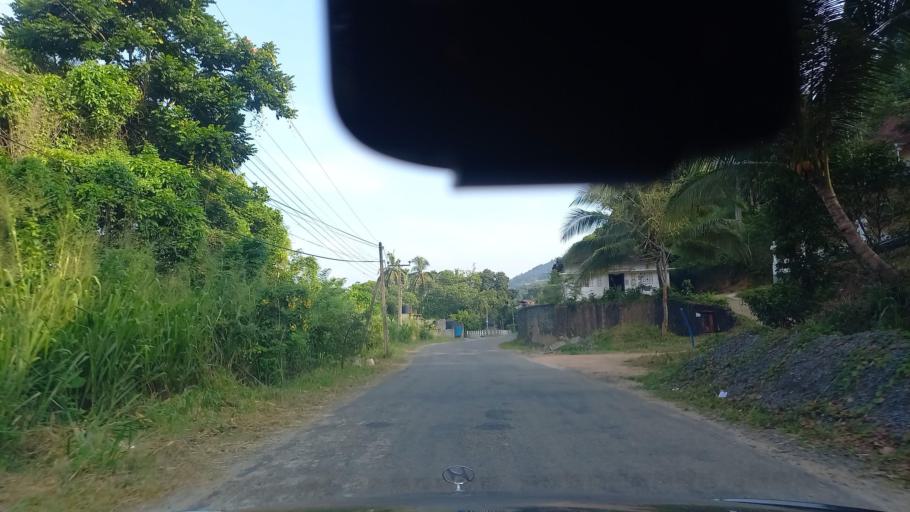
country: LK
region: Central
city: Gampola
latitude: 7.2270
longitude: 80.6037
